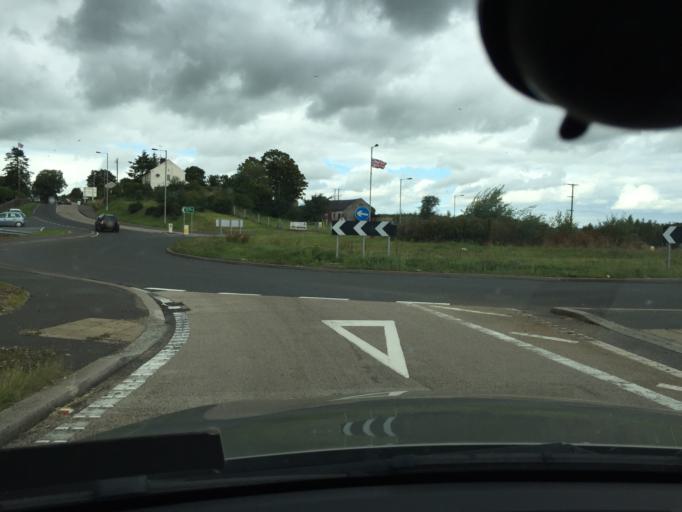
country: GB
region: Northern Ireland
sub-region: Newry and Mourne District
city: Newry
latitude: 54.1998
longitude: -6.3620
